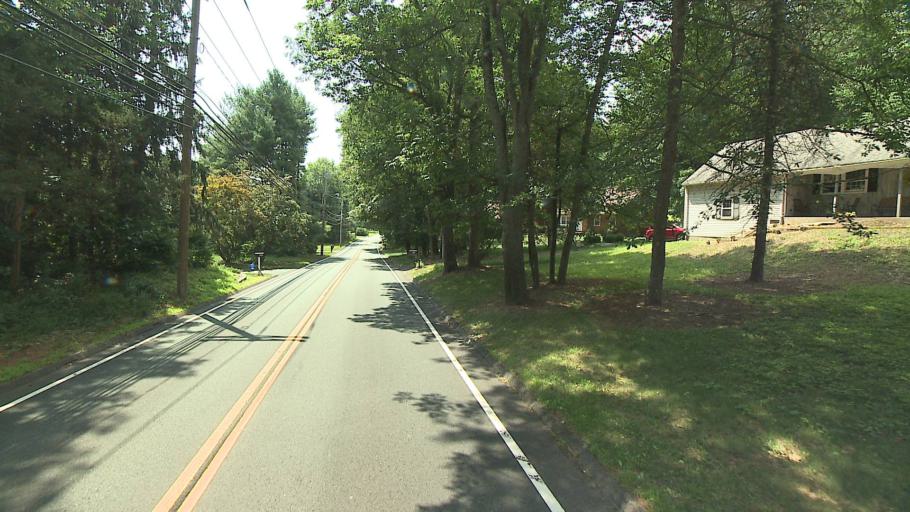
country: US
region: Connecticut
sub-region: Hartford County
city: Collinsville
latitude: 41.7787
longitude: -72.8904
